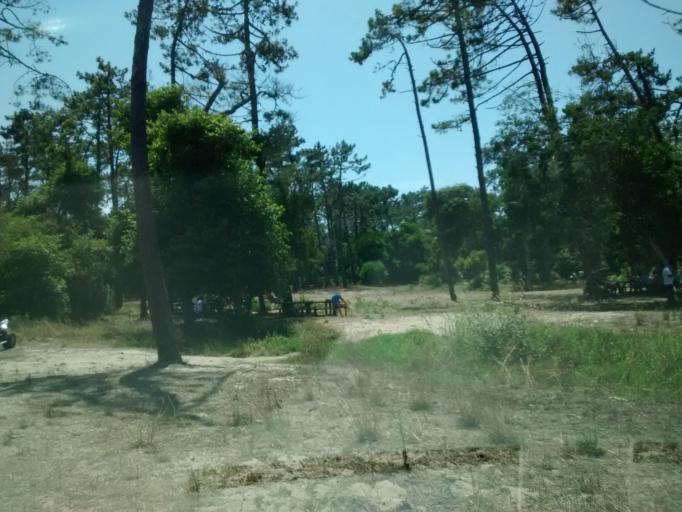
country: PT
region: Coimbra
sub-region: Mira
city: Mira
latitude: 40.4438
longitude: -8.7977
